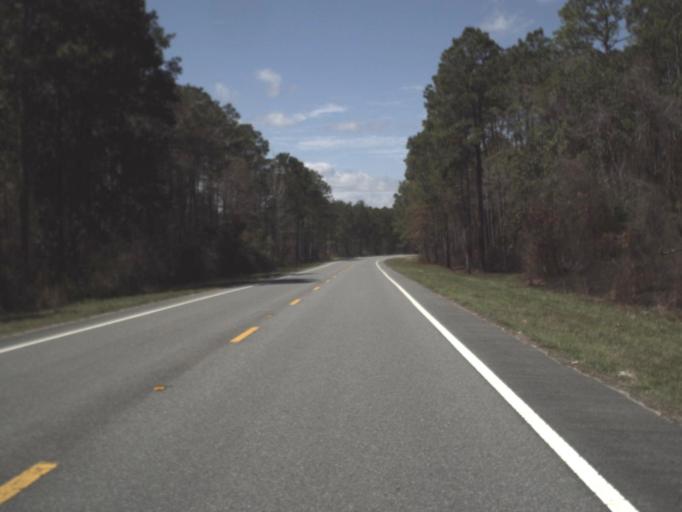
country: US
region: Florida
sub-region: Gadsden County
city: Midway
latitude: 30.3572
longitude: -84.5275
